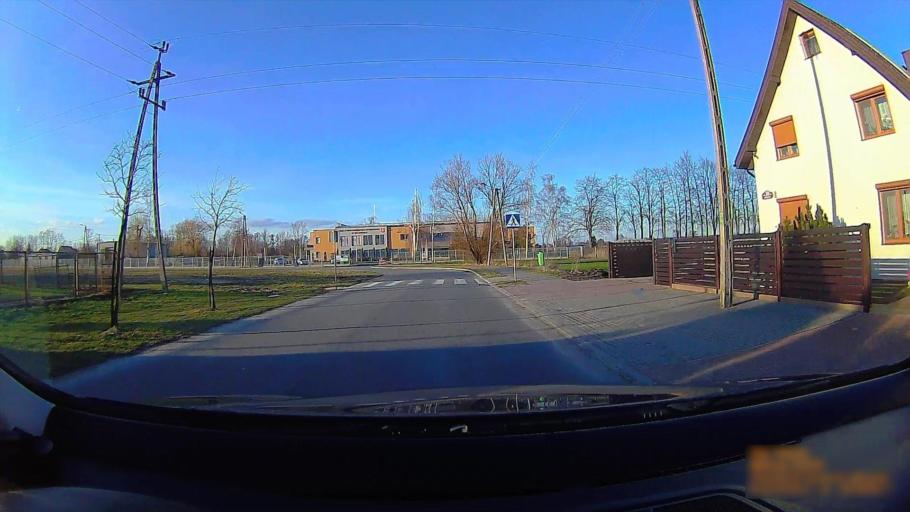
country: PL
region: Greater Poland Voivodeship
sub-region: Powiat koninski
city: Rychwal
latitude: 52.0754
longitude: 18.1656
